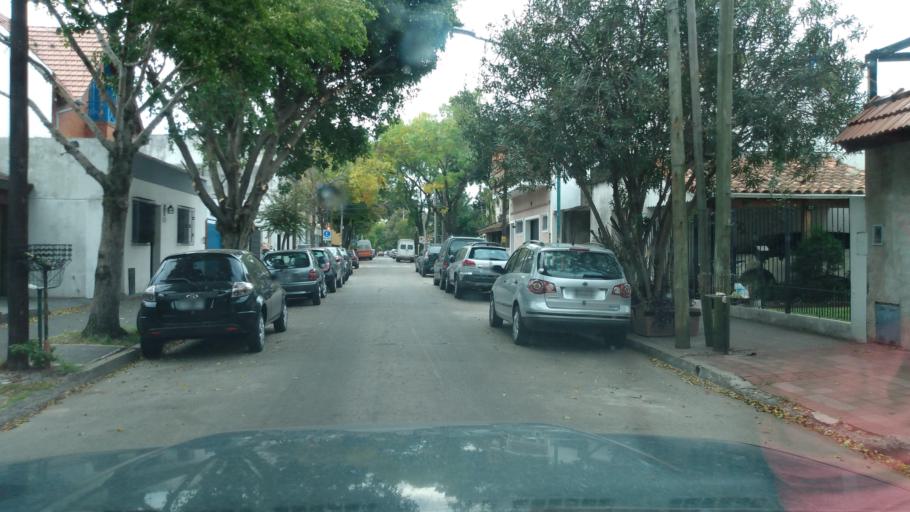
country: AR
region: Buenos Aires
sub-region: Partido de Vicente Lopez
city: Olivos
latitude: -34.5077
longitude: -58.4997
